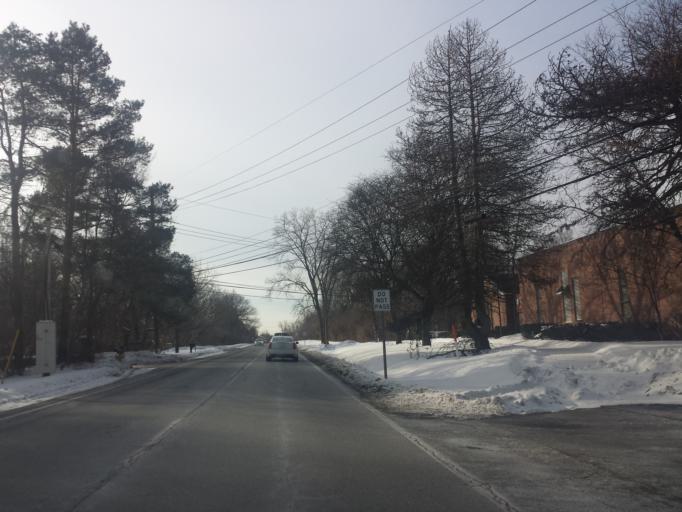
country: US
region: Michigan
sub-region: Oakland County
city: Franklin
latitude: 42.5364
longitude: -83.3408
